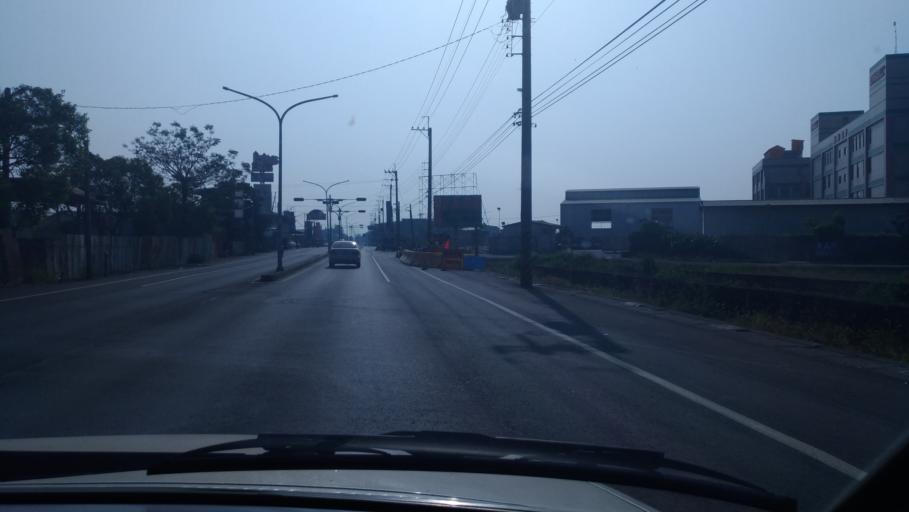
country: TW
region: Taiwan
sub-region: Chiayi
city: Jiayi Shi
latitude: 23.5211
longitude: 120.4248
